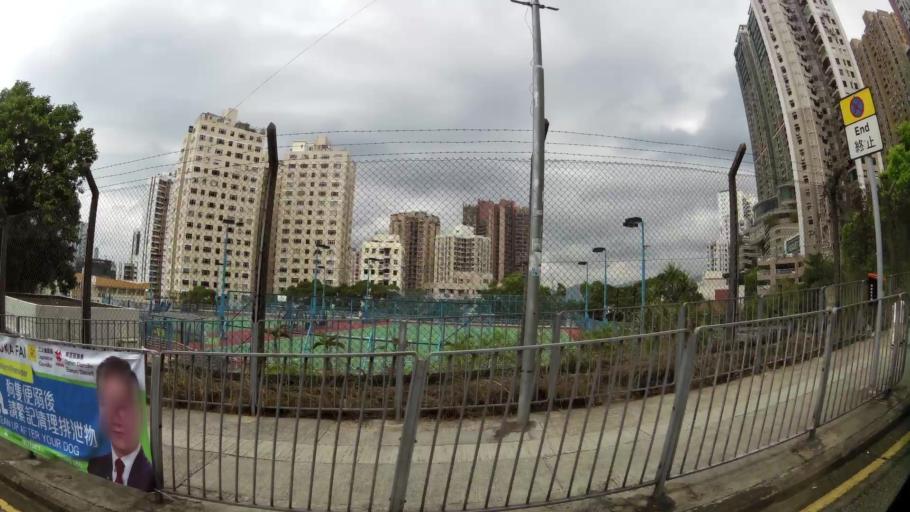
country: HK
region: Wanchai
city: Wan Chai
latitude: 22.2846
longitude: 114.1954
